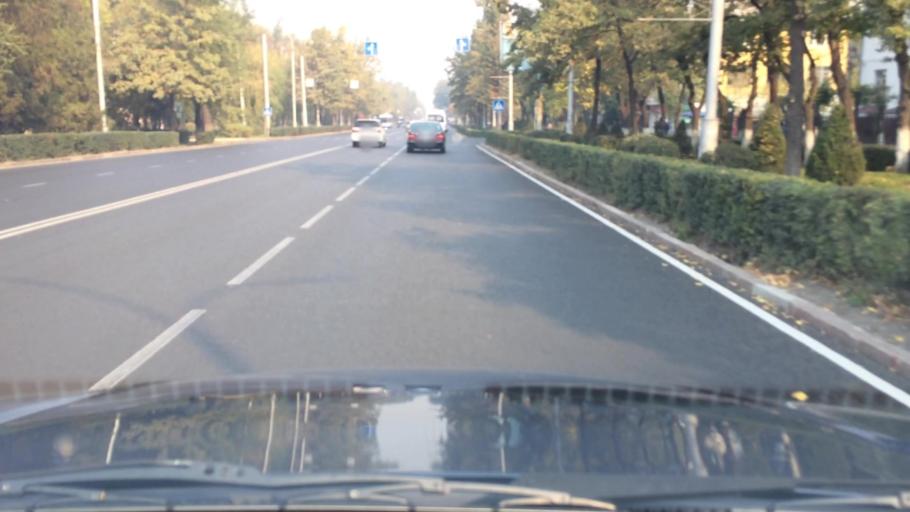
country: KG
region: Chuy
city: Bishkek
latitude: 42.8459
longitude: 74.5863
